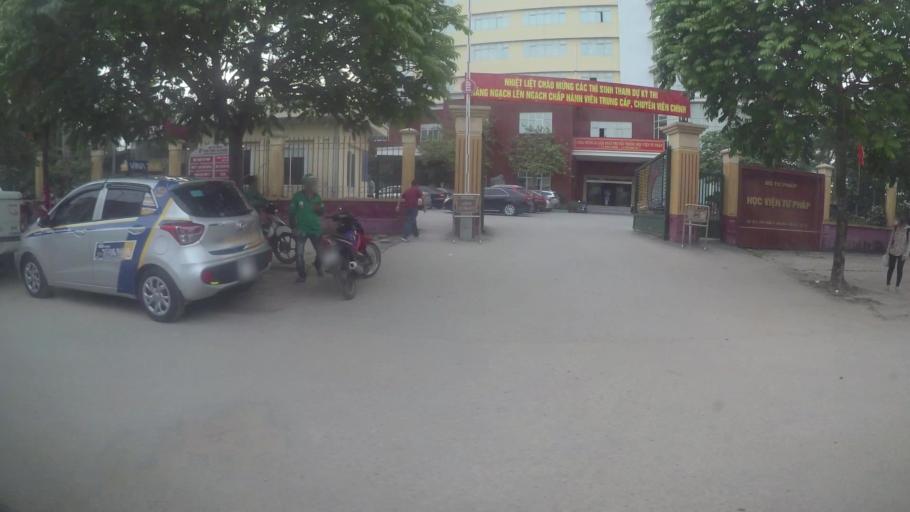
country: VN
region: Ha Noi
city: Cau Dien
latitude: 21.0454
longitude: 105.7745
